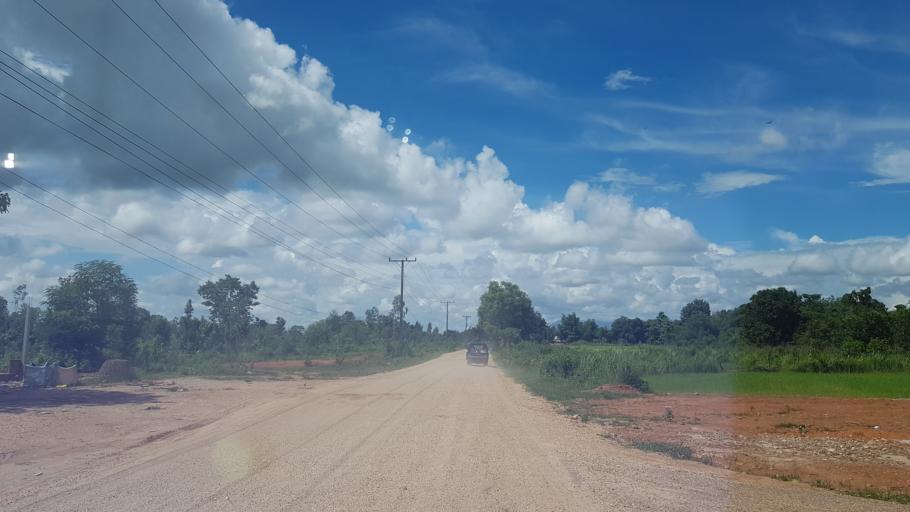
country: LA
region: Vientiane
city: Vientiane
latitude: 18.2295
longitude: 102.5251
